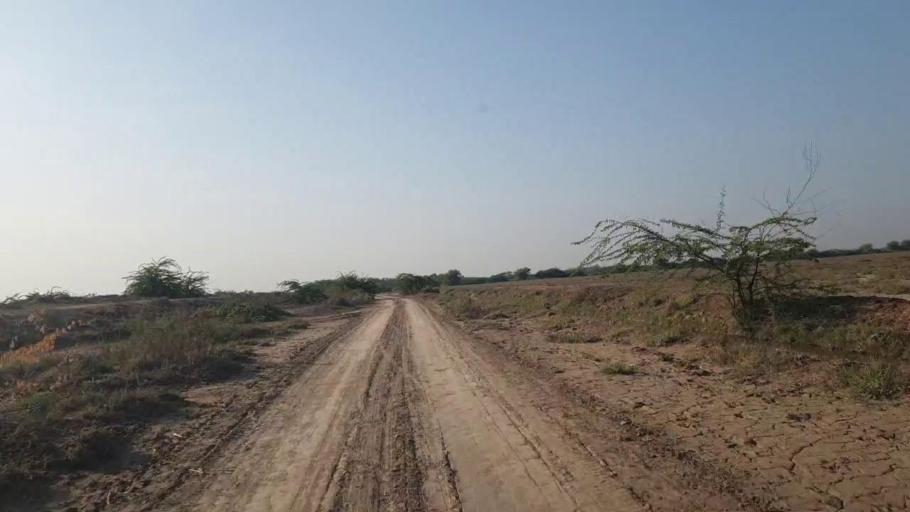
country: PK
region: Sindh
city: Badin
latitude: 24.4619
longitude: 68.7367
